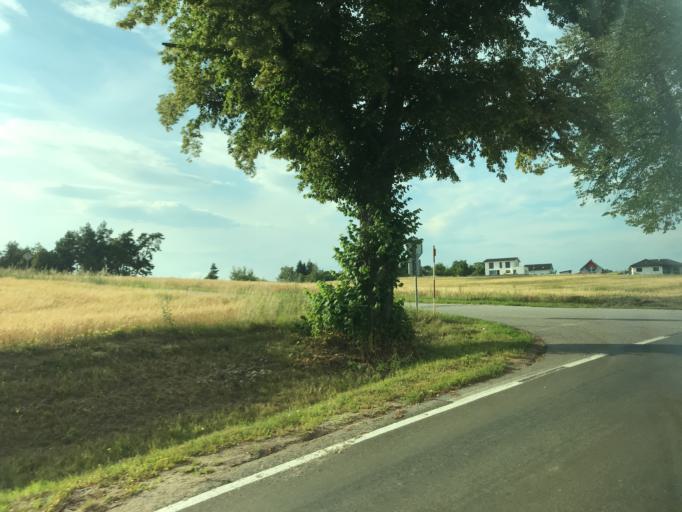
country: CZ
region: Jihocesky
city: Rudolfov
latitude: 49.0019
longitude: 14.5529
